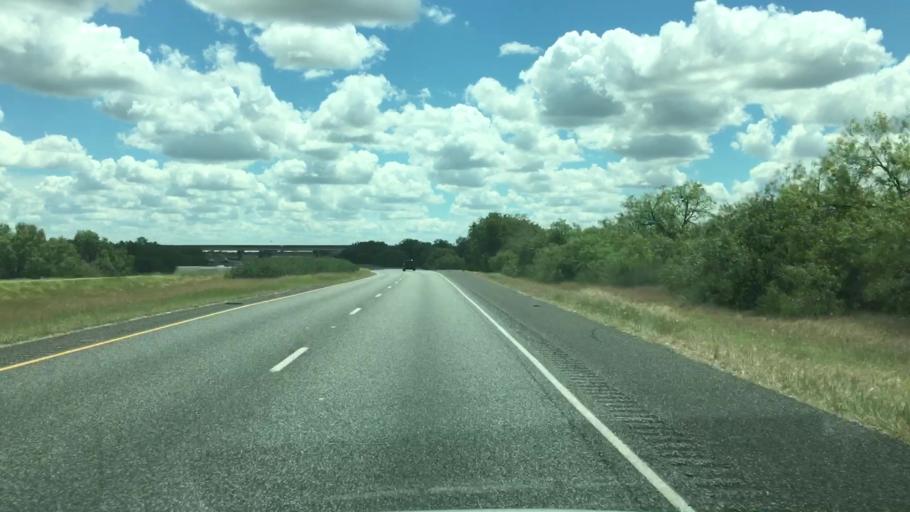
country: US
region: Texas
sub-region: Atascosa County
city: Pleasanton
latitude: 28.9133
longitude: -98.4348
